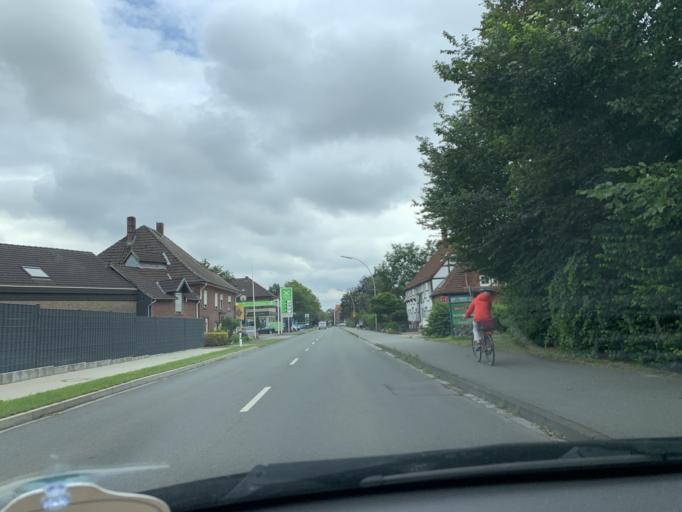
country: DE
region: North Rhine-Westphalia
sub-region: Regierungsbezirk Munster
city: Wadersloh
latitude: 51.7426
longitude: 8.2431
